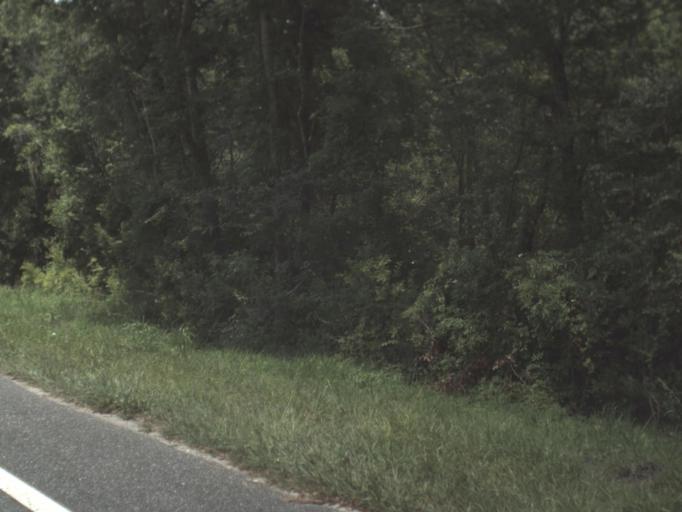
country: US
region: Florida
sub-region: Hamilton County
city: Jasper
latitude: 30.5531
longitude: -83.0628
